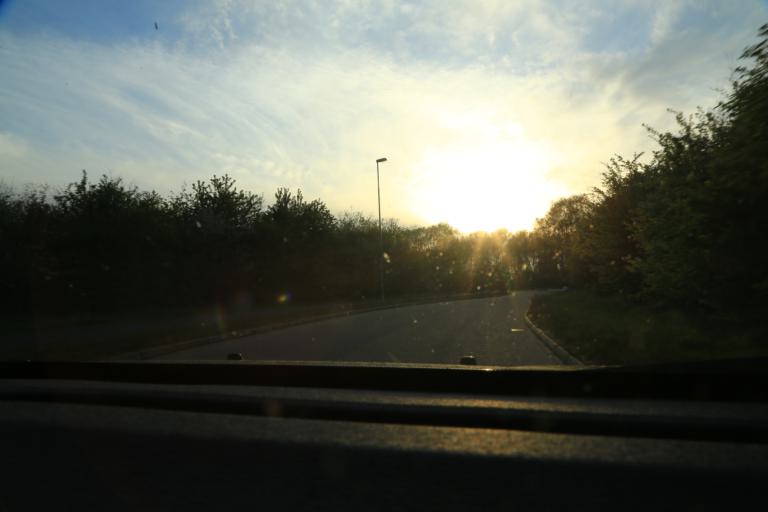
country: SE
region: Halland
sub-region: Varbergs Kommun
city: Traslovslage
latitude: 57.0630
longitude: 12.2861
